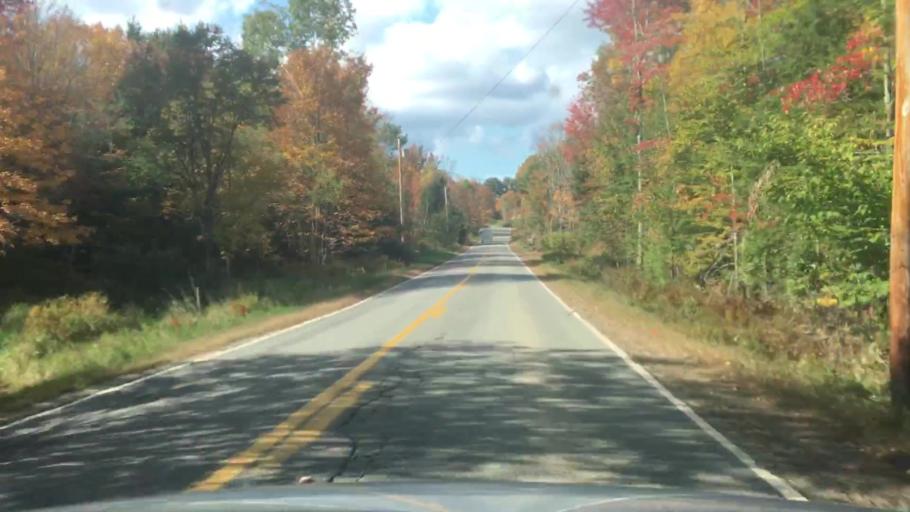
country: US
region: Maine
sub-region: Knox County
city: Washington
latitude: 44.3032
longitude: -69.3315
